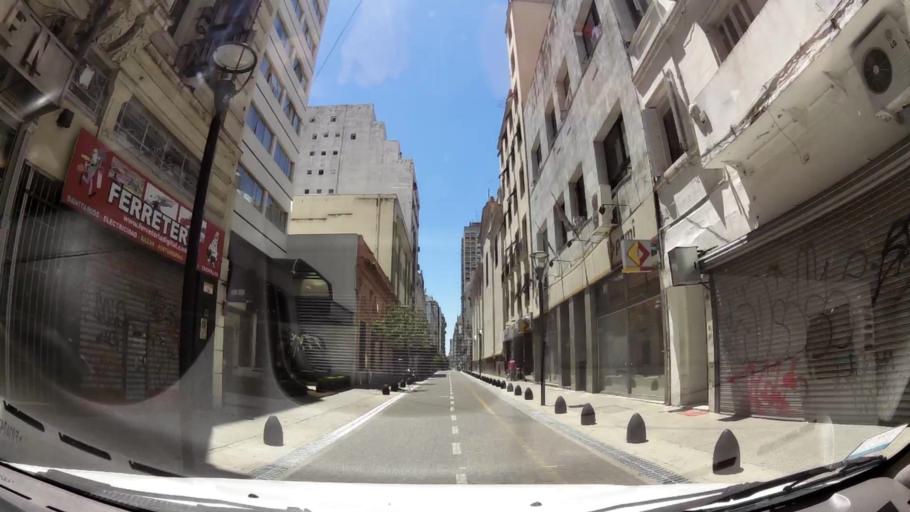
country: AR
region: Buenos Aires F.D.
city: Buenos Aires
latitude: -34.6081
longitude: -58.3794
